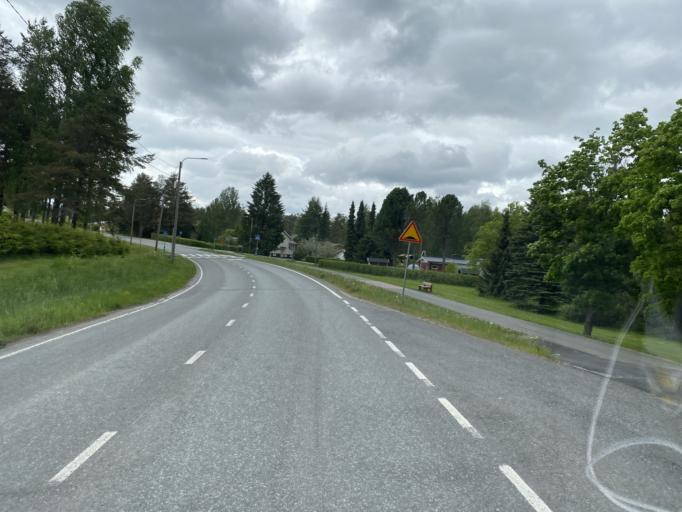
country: FI
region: Pirkanmaa
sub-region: Etelae-Pirkanmaa
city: Urjala
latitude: 61.0791
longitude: 23.5645
